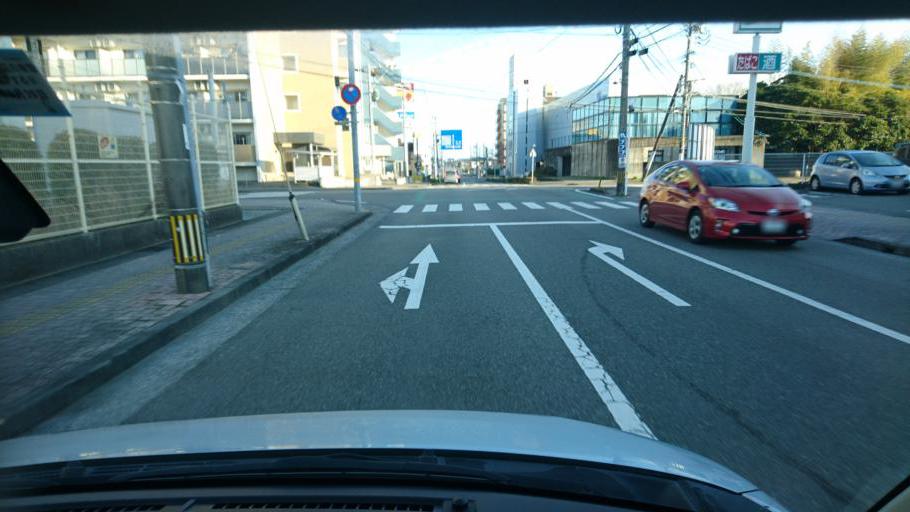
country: JP
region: Miyazaki
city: Miyazaki-shi
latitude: 31.8299
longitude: 131.4201
